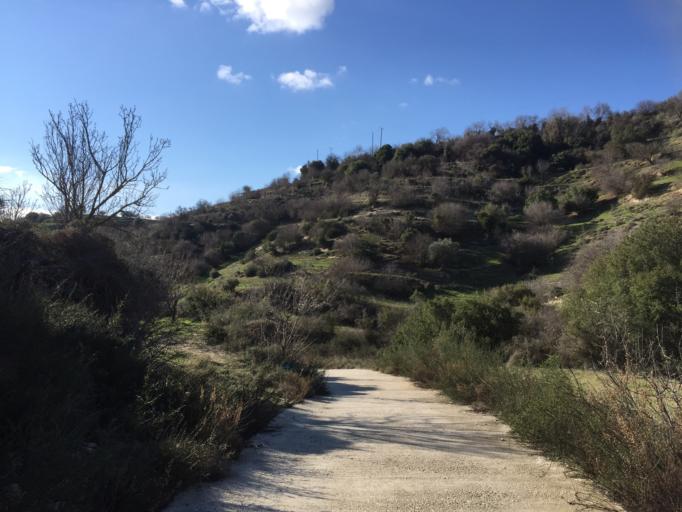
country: CY
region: Pafos
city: Mesogi
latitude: 34.8349
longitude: 32.5126
